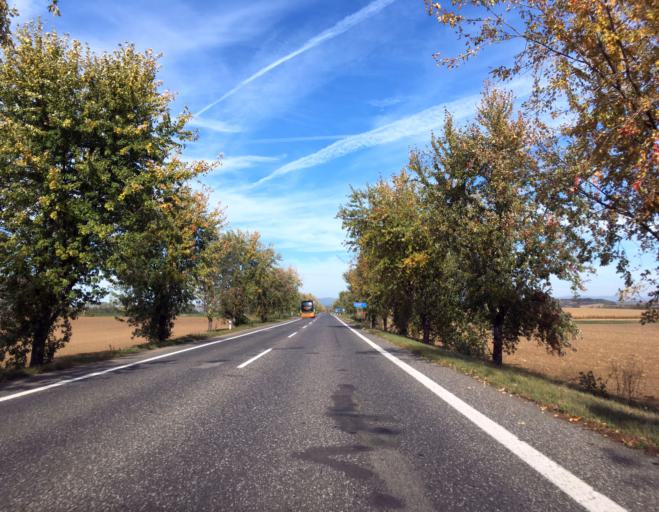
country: SK
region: Banskobystricky
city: Dudince
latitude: 48.1319
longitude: 18.8765
